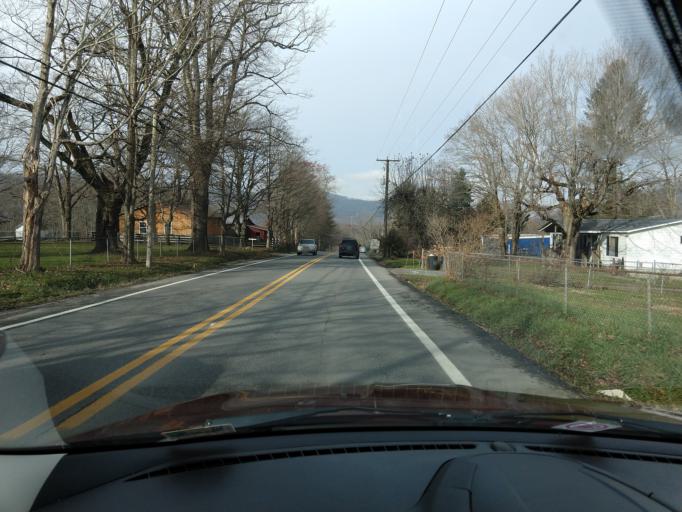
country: US
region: West Virginia
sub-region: Greenbrier County
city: Rainelle
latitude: 37.9539
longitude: -80.6766
